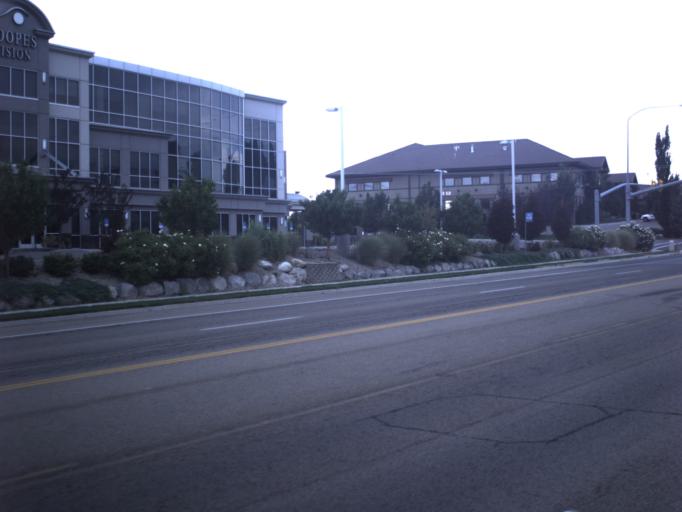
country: US
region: Utah
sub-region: Salt Lake County
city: Draper
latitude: 40.5362
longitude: -111.8913
